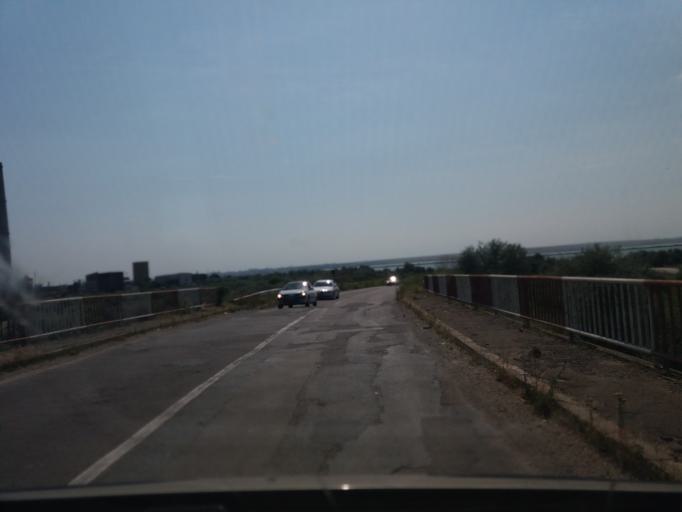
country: RO
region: Constanta
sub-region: Comuna Corbu
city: Corbu
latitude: 44.3523
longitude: 28.6531
